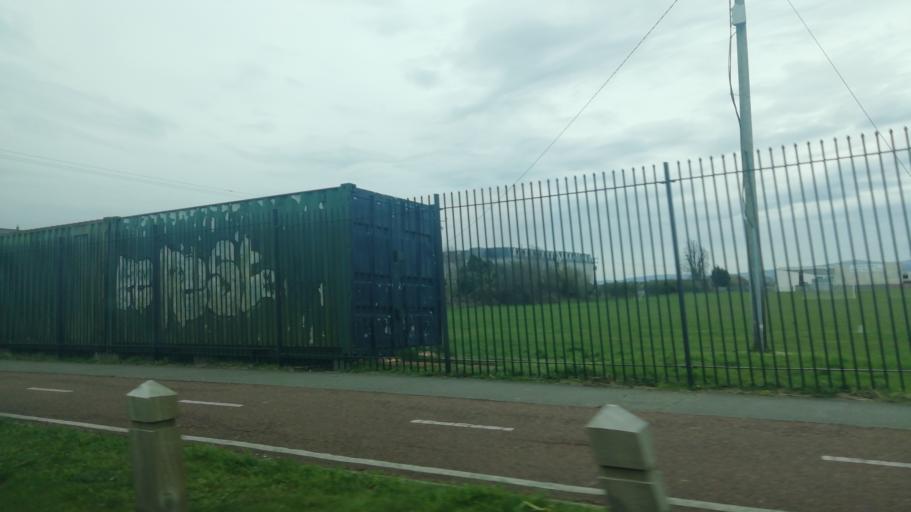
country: IE
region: Leinster
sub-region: Kildare
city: Celbridge
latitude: 53.3356
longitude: -6.5609
